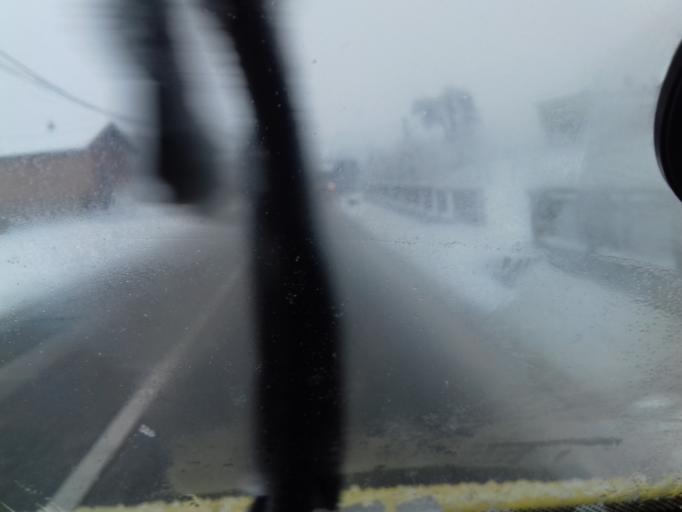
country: BA
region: Federation of Bosnia and Herzegovina
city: Busovaca
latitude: 44.1378
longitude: 17.8518
